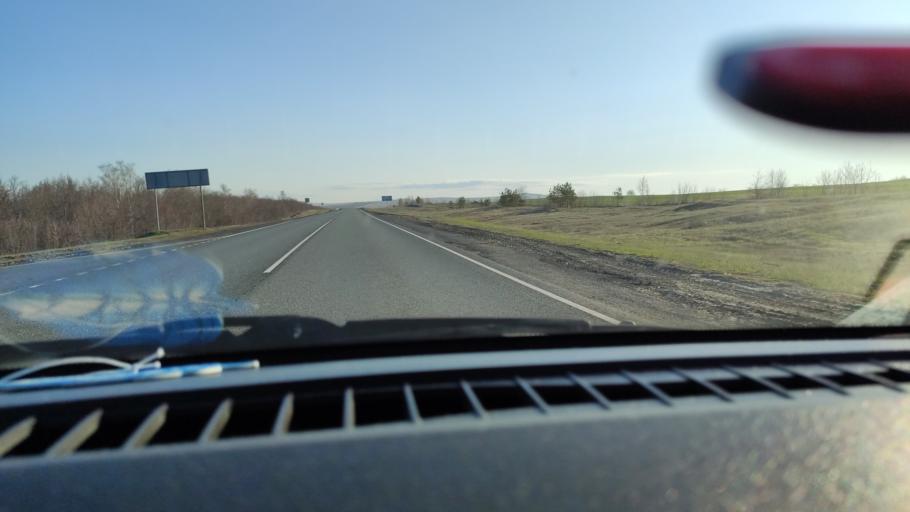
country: RU
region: Saratov
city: Balakovo
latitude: 52.1781
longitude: 47.8387
